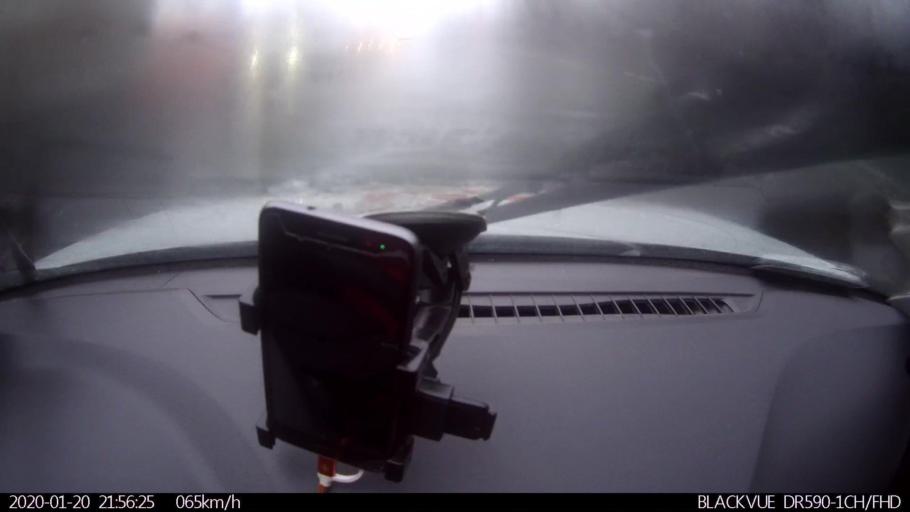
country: RU
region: Nizjnij Novgorod
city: Gorbatovka
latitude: 56.3141
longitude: 43.8441
